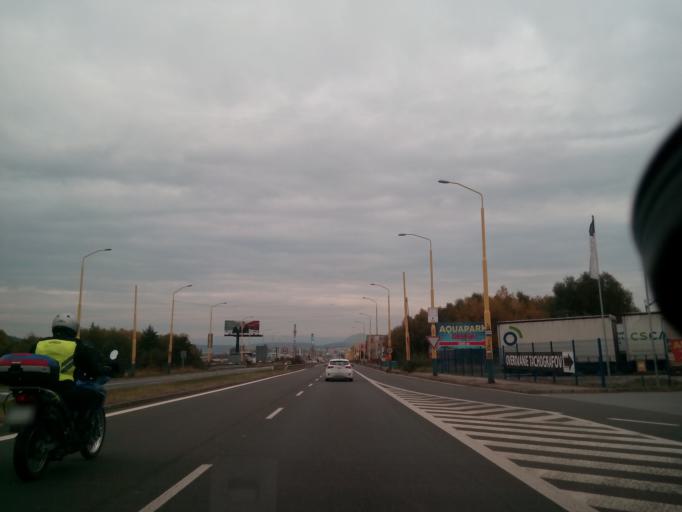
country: SK
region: Presovsky
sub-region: Okres Presov
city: Presov
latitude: 48.9601
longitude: 21.2564
